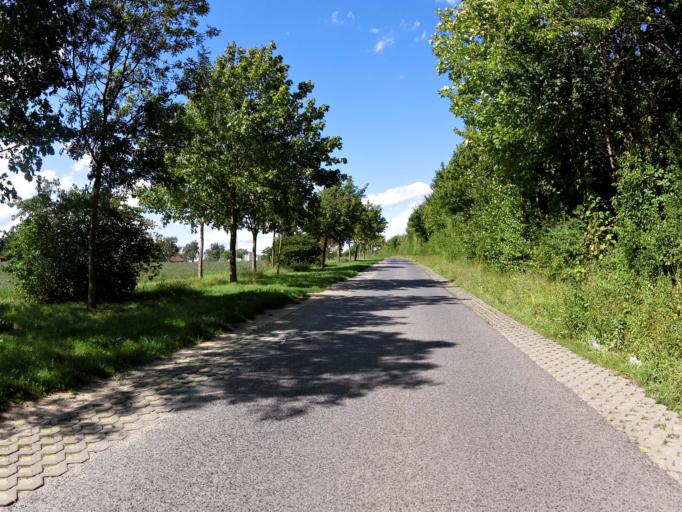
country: DE
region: Bavaria
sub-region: Regierungsbezirk Unterfranken
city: Marktsteft
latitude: 49.6917
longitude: 10.1437
